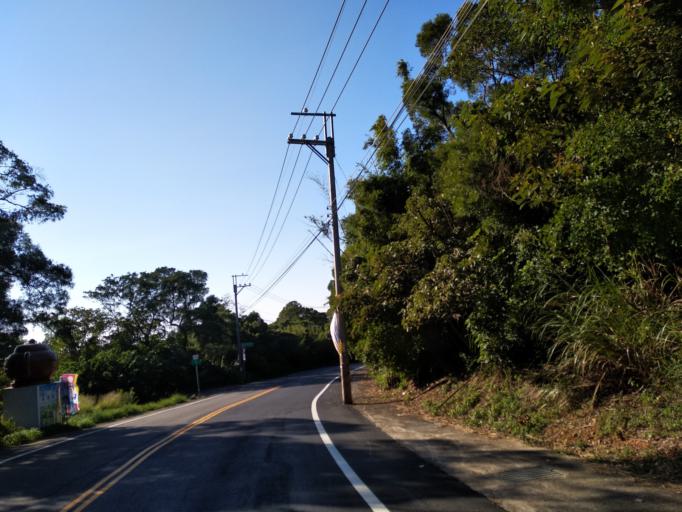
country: TW
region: Taiwan
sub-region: Hsinchu
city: Zhubei
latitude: 24.8725
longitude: 121.0585
